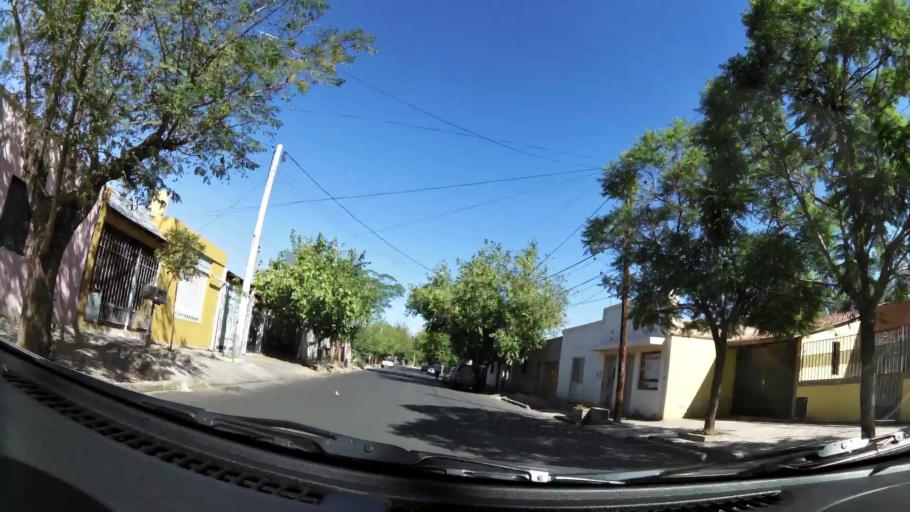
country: AR
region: San Juan
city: San Juan
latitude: -31.5417
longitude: -68.5496
